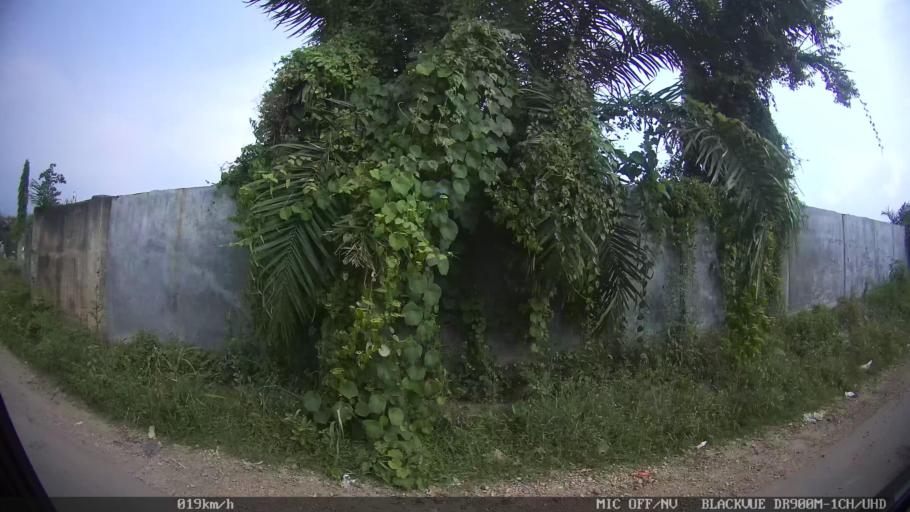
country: ID
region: Lampung
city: Kedaton
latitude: -5.3532
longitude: 105.2238
